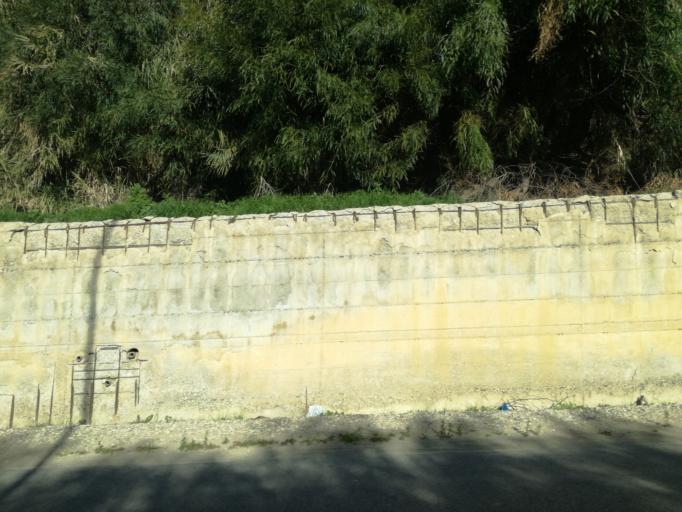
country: IT
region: Sicily
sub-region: Provincia di Caltanissetta
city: Gela
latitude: 37.0683
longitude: 14.2283
